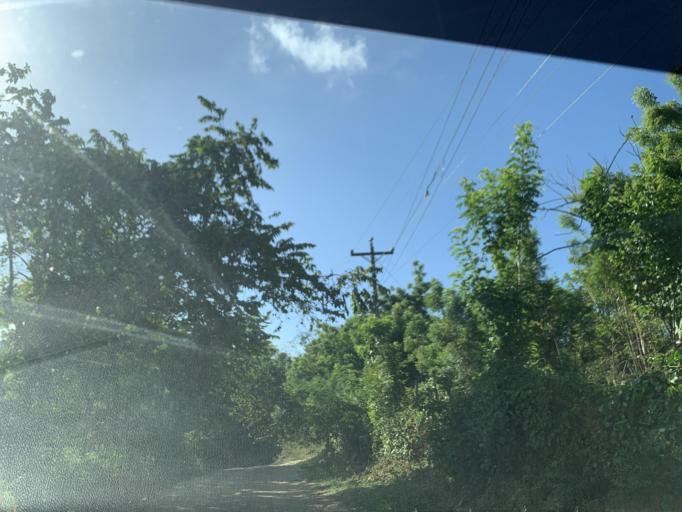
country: DO
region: Puerto Plata
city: Luperon
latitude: 19.8893
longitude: -70.8882
